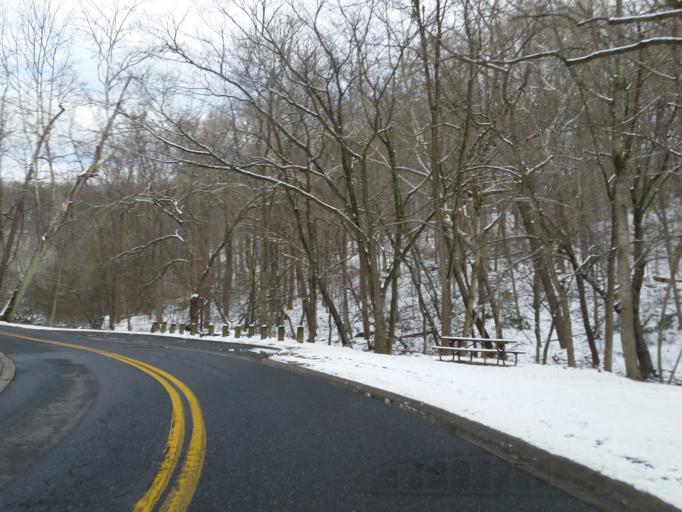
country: US
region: Maryland
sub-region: Montgomery County
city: Chevy Chase
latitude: 38.9460
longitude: -77.0462
